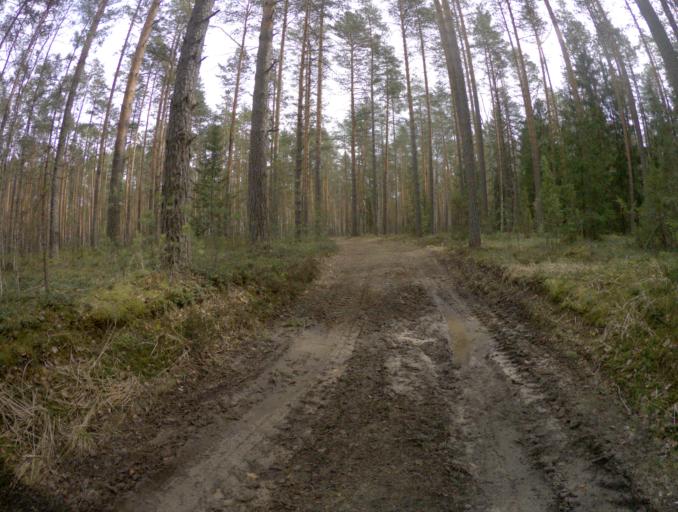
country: RU
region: Vladimir
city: Raduzhnyy
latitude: 55.9477
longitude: 40.2824
